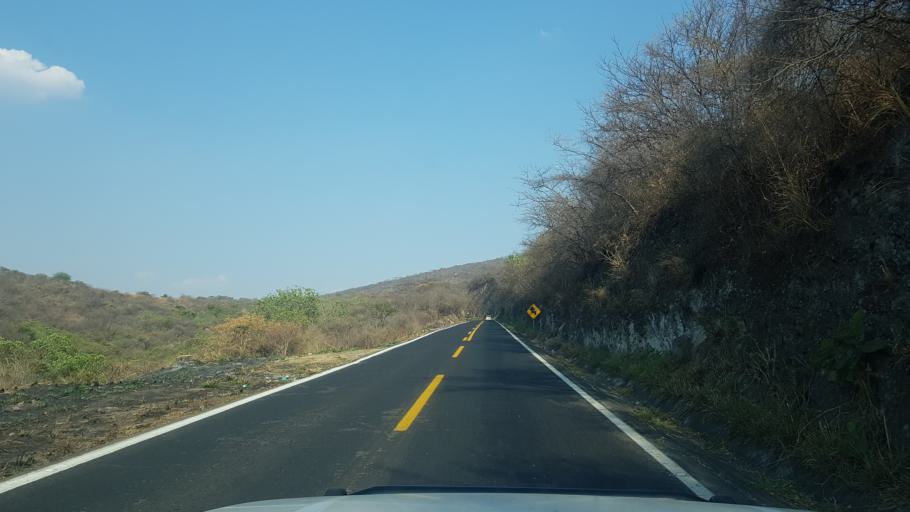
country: MX
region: Puebla
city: Calmeca
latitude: 18.6508
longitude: -98.6678
